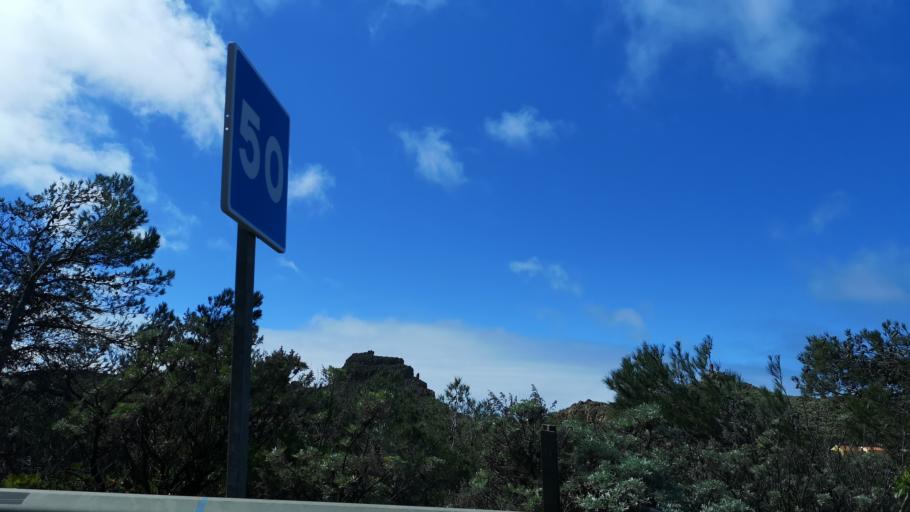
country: ES
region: Canary Islands
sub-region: Provincia de Santa Cruz de Tenerife
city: Vallehermosa
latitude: 28.1304
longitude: -17.3206
